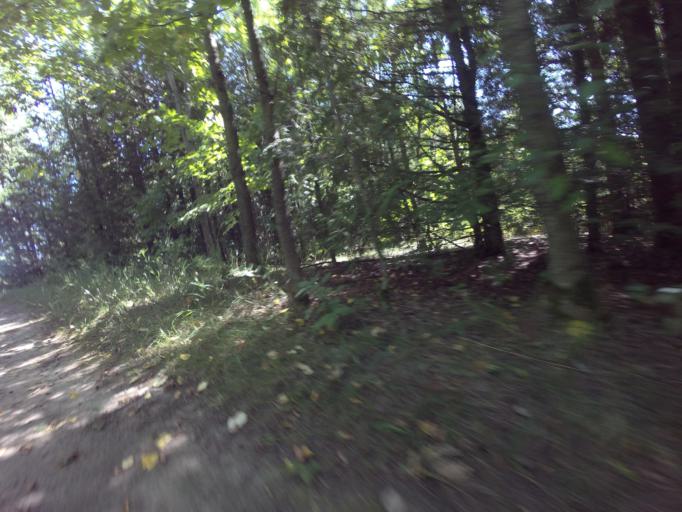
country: CA
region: Ontario
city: Orangeville
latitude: 43.8207
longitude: -80.0206
